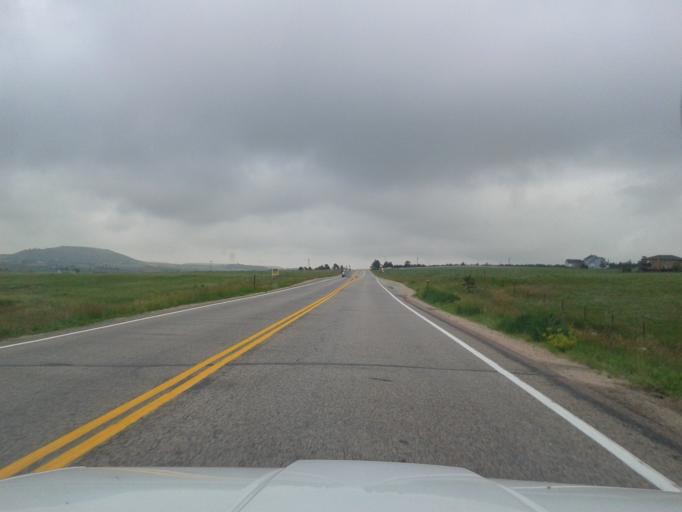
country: US
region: Colorado
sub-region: El Paso County
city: Woodmoor
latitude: 39.1248
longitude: -104.7665
